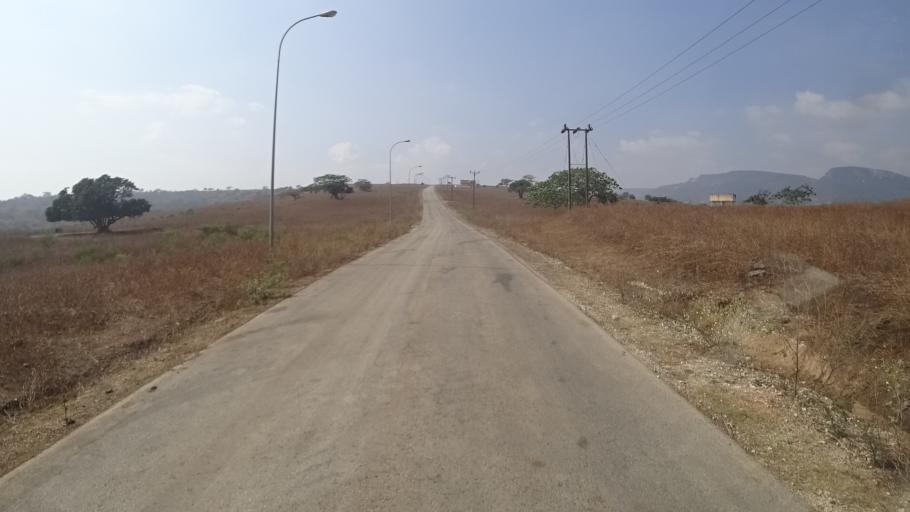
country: YE
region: Al Mahrah
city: Hawf
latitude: 16.7298
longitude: 53.2724
